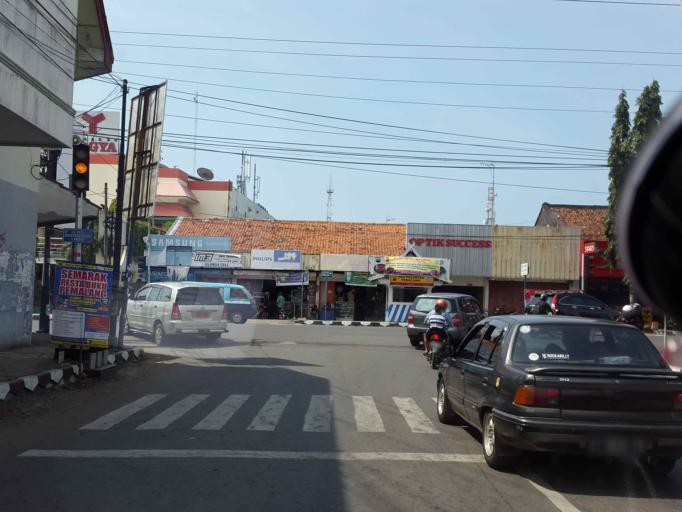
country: ID
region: Central Java
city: Pemalang
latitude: -6.8906
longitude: 109.3885
